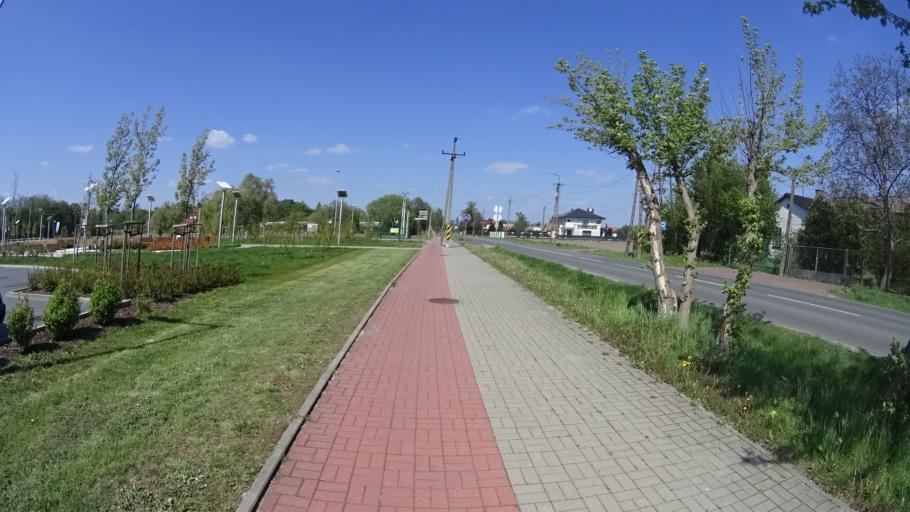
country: PL
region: Masovian Voivodeship
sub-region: Powiat warszawski zachodni
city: Stare Babice
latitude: 52.2479
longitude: 20.8200
